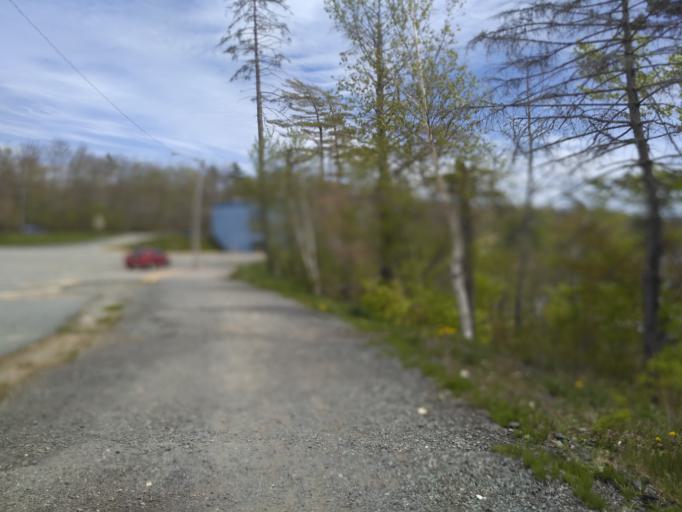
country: CA
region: Nova Scotia
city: Dartmouth
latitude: 44.7768
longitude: -63.6693
